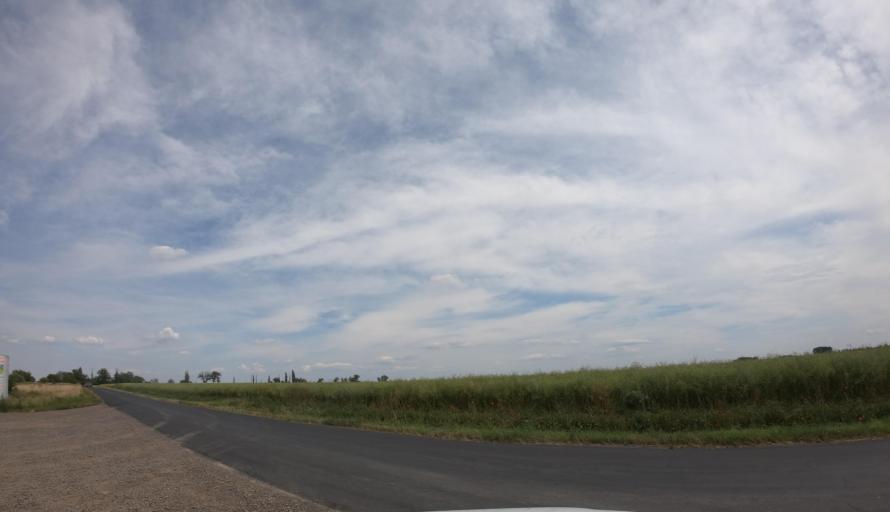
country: PL
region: West Pomeranian Voivodeship
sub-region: Powiat pyrzycki
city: Kozielice
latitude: 53.1235
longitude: 14.8442
